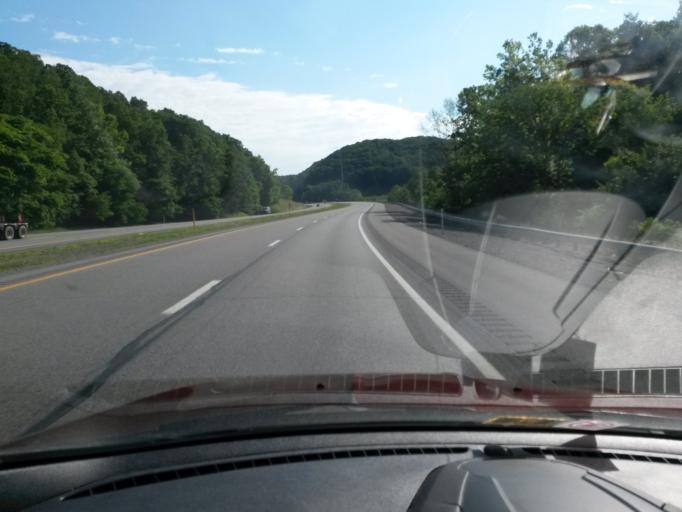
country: US
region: West Virginia
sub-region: Braxton County
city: Sutton
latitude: 38.7686
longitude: -80.6801
